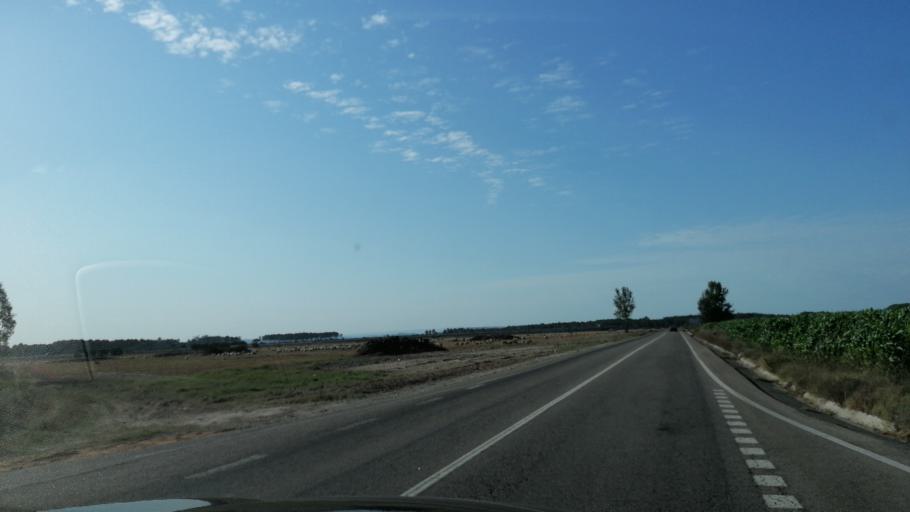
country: PT
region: Santarem
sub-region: Almeirim
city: Fazendas de Almeirim
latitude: 39.1528
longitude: -8.6190
